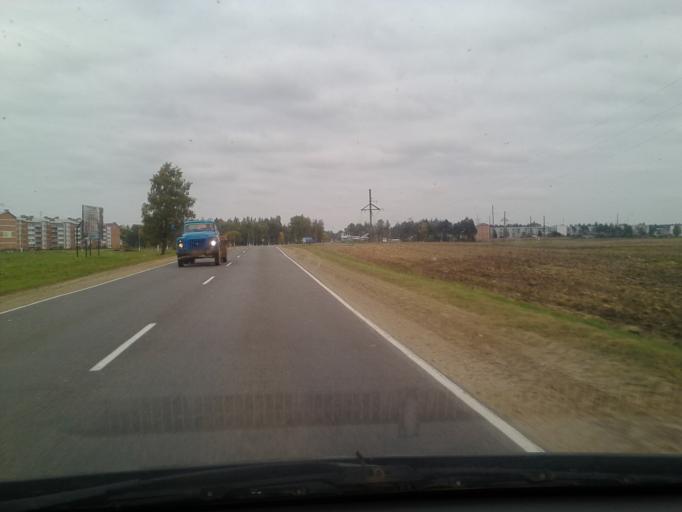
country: BY
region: Vitebsk
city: Pastavy
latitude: 55.1060
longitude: 26.8739
